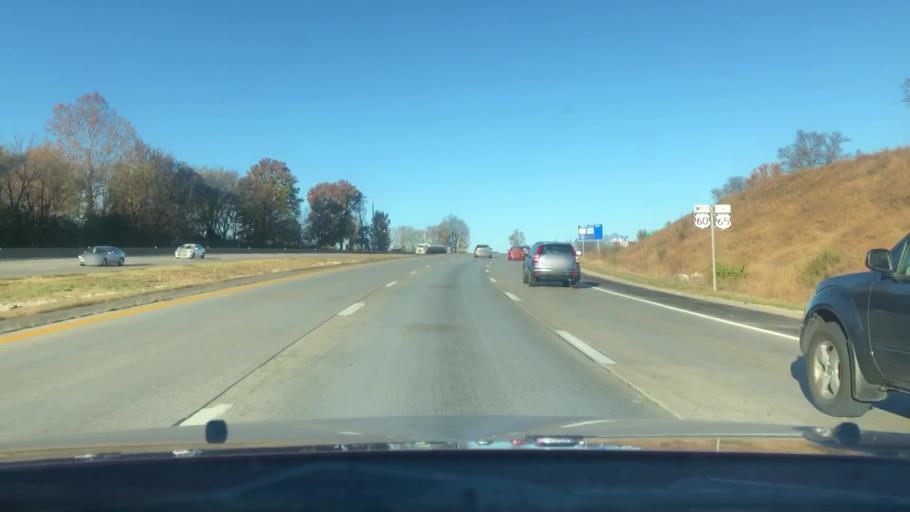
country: US
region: Missouri
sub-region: Greene County
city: Springfield
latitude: 37.1312
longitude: -93.2412
